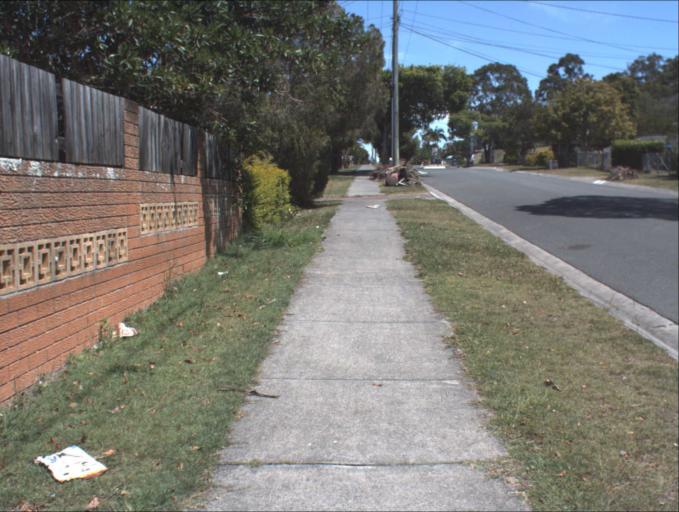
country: AU
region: Queensland
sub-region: Logan
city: Logan City
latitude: -27.6465
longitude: 153.1271
